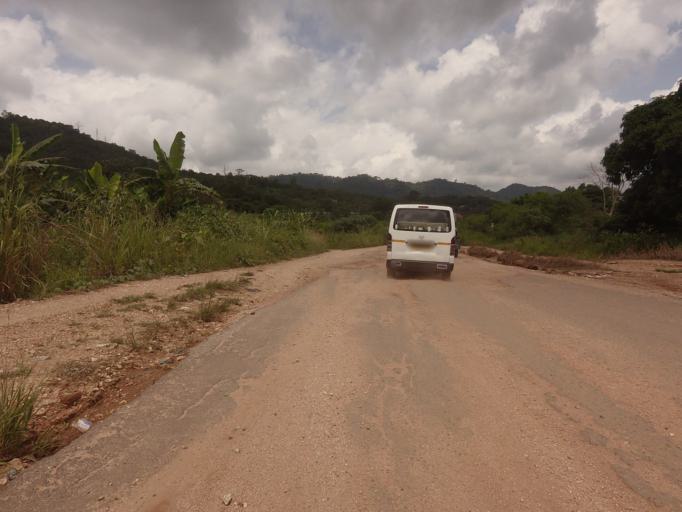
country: GH
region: Volta
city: Ho
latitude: 6.6942
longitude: 0.3359
